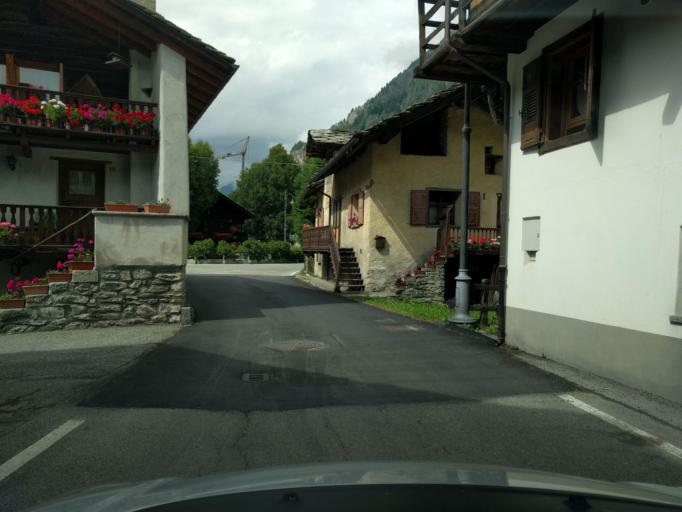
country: IT
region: Aosta Valley
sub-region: Valle d'Aosta
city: Gressoney-Saint-Jean
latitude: 45.7696
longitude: 7.8266
